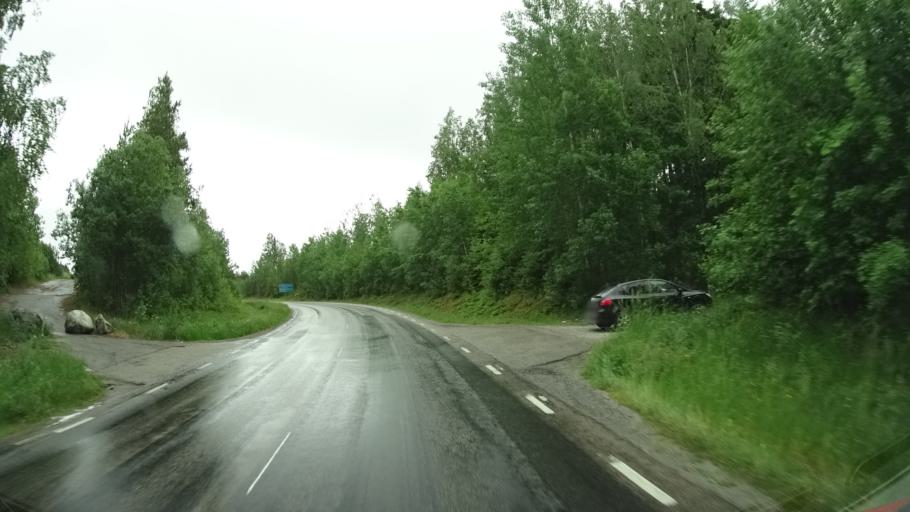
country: SE
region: Soedermanland
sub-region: Nykopings Kommun
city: Stigtomta
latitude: 58.7529
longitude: 16.7298
